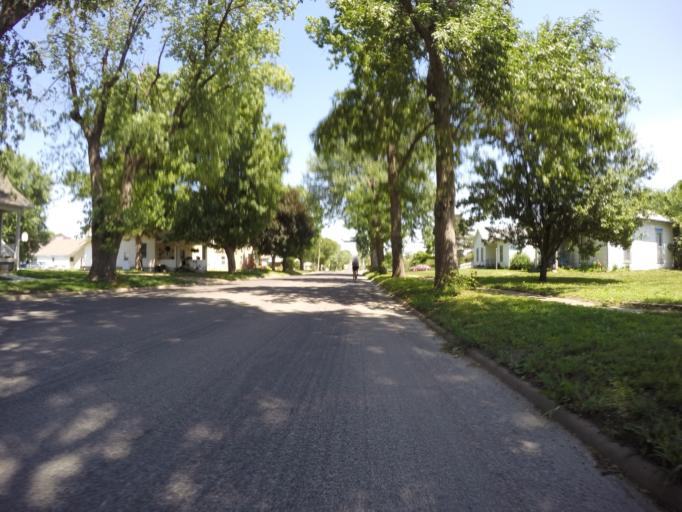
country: US
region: Kansas
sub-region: Nemaha County
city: Sabetha
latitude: 39.8997
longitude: -95.7985
